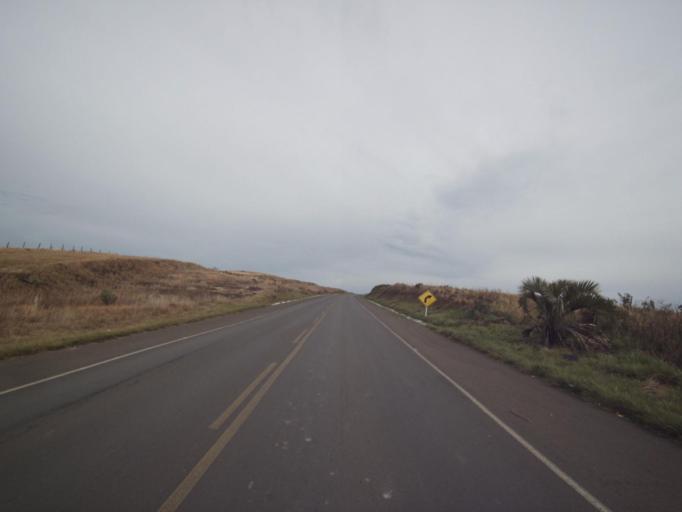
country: BR
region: Parana
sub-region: Palmas
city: Palmas
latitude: -26.7626
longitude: -51.6679
